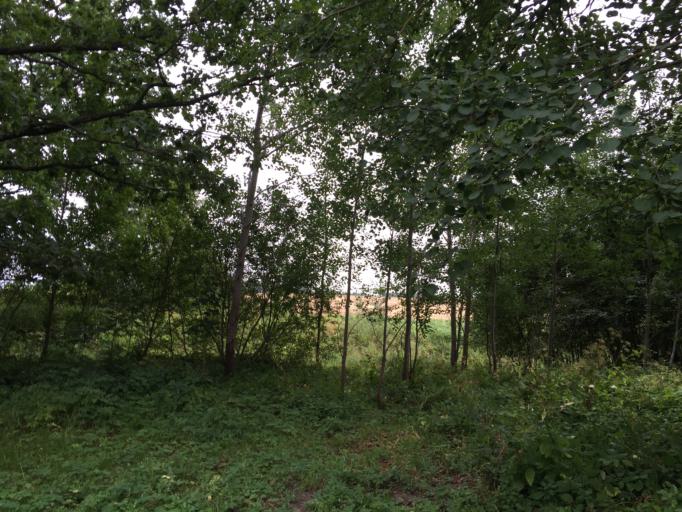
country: LV
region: Dobeles Rajons
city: Dobele
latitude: 56.7135
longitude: 23.1851
